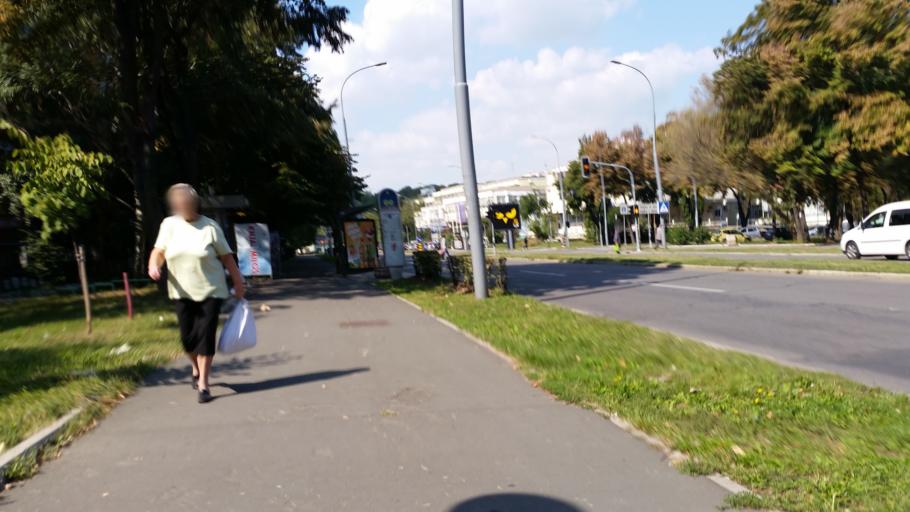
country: RS
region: Central Serbia
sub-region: Belgrade
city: Zemun
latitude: 44.8286
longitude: 20.4024
